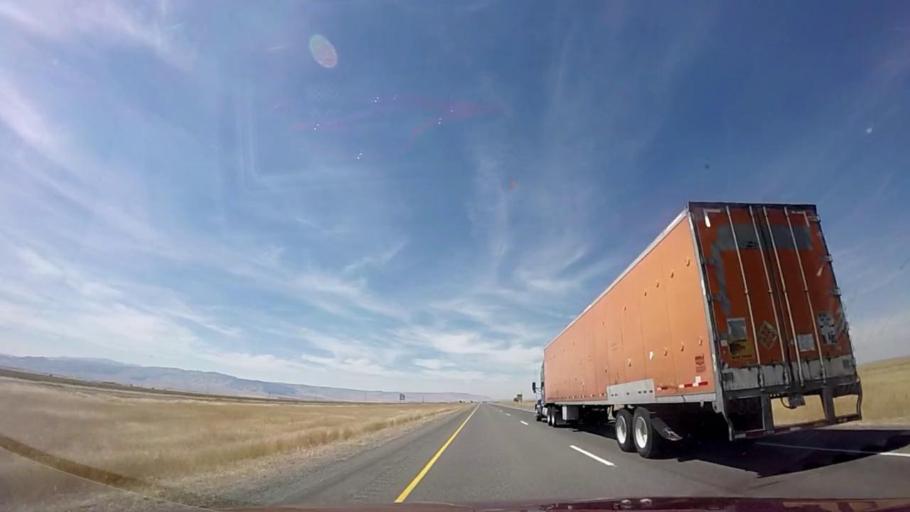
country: US
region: Idaho
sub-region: Minidoka County
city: Rupert
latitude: 42.3387
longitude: -113.2282
